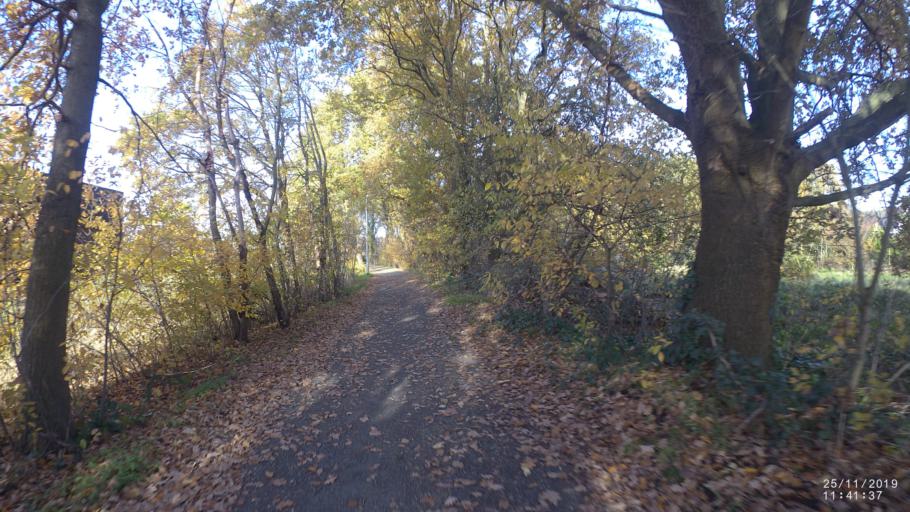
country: BE
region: Flanders
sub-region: Provincie Vlaams-Brabant
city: Aarschot
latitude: 51.0017
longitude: 4.8393
